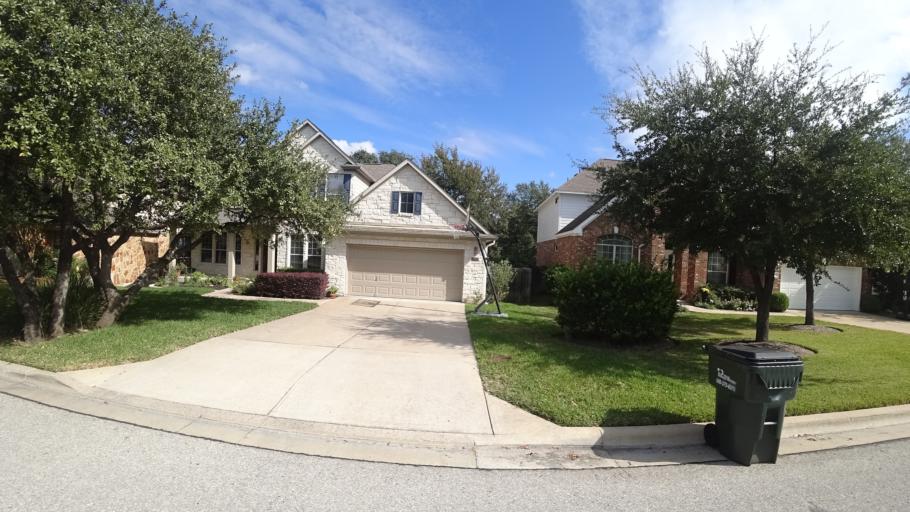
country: US
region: Texas
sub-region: Travis County
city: Hudson Bend
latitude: 30.3690
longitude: -97.9020
